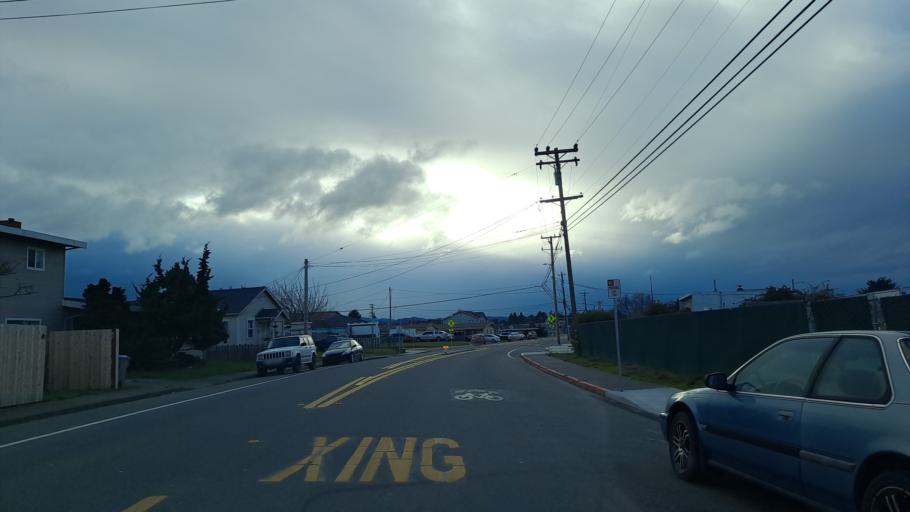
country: US
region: California
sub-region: Humboldt County
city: Fortuna
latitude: 40.5888
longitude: -124.1437
